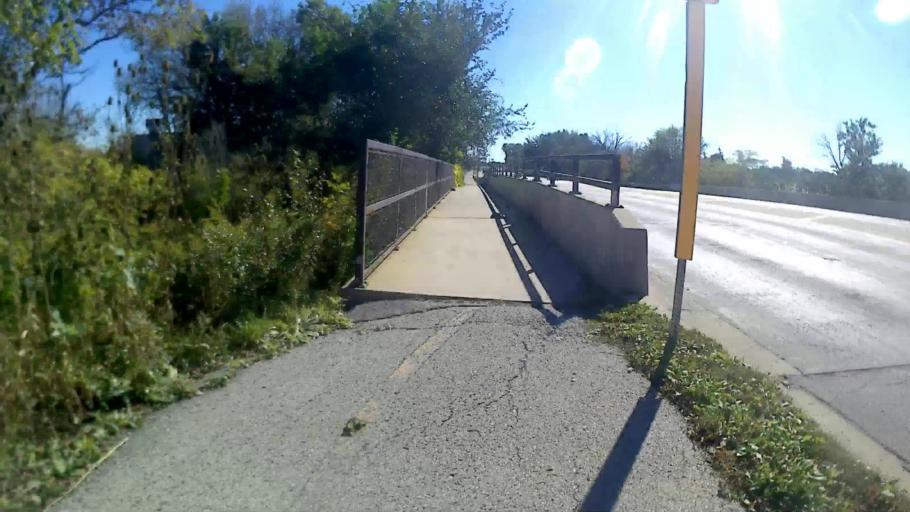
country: US
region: Illinois
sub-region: DuPage County
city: Itasca
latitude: 41.9723
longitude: -87.9980
